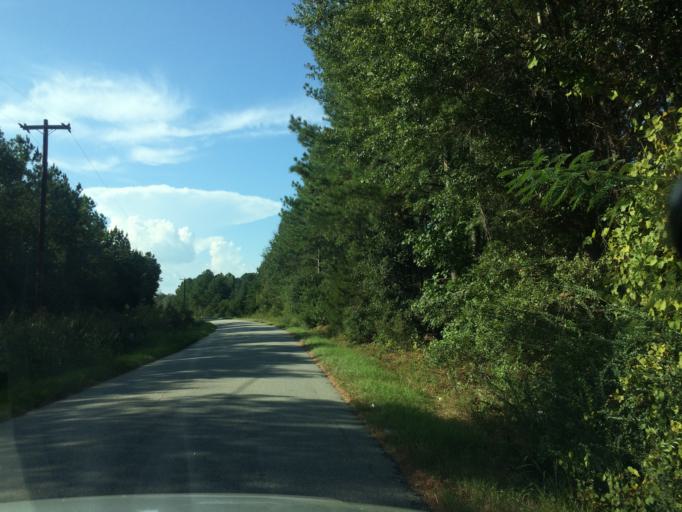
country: US
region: South Carolina
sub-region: Laurens County
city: Laurens
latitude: 34.5768
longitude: -82.0938
